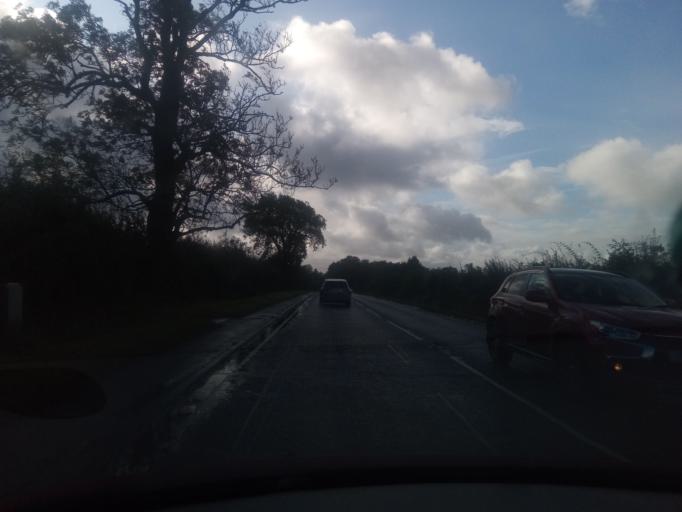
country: GB
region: England
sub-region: Cumbria
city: Carlisle
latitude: 54.9482
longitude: -2.9433
